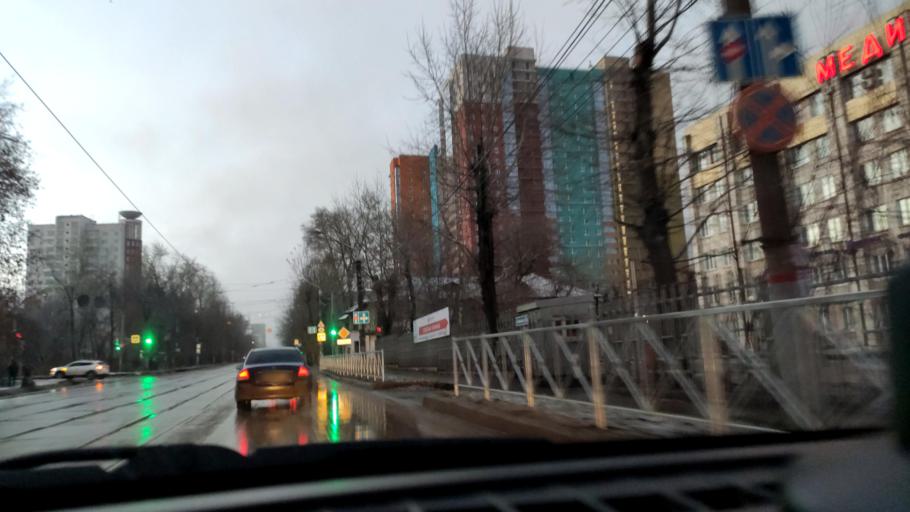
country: RU
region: Perm
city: Perm
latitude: 57.9908
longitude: 56.2179
